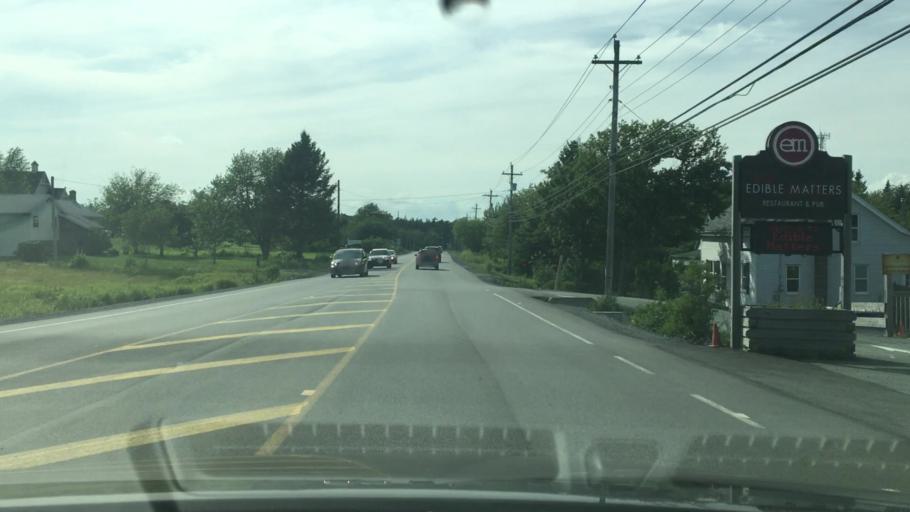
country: CA
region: Nova Scotia
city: Dartmouth
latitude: 44.7271
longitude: -63.7446
